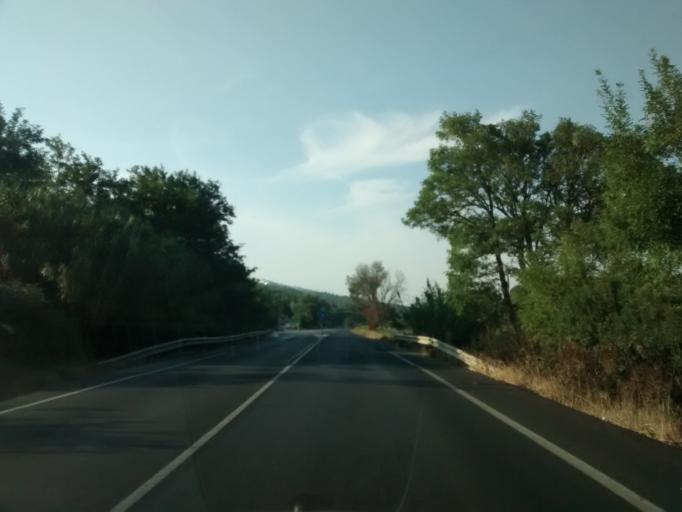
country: ES
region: Andalusia
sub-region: Provincia de Cadiz
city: Vejer de la Frontera
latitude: 36.2310
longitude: -5.9488
